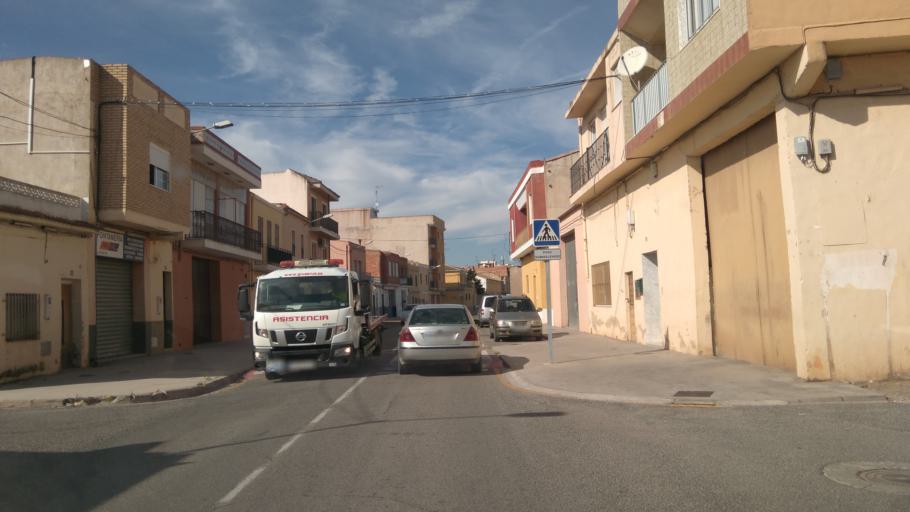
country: ES
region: Valencia
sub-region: Provincia de Valencia
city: Real de Montroi
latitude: 39.3338
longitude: -0.6066
